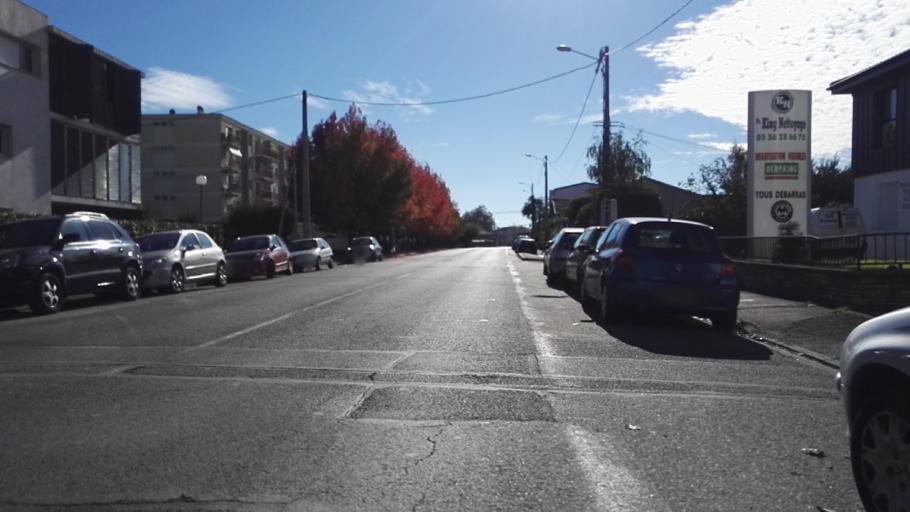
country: FR
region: Aquitaine
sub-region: Departement de la Gironde
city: Merignac
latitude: 44.8549
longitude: -0.6442
